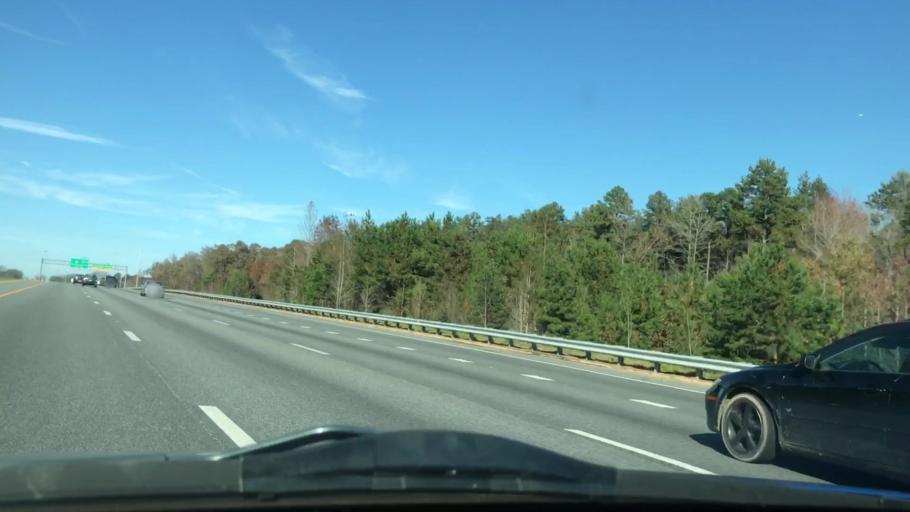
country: US
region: North Carolina
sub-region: Guilford County
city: High Point
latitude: 35.9766
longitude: -79.9741
